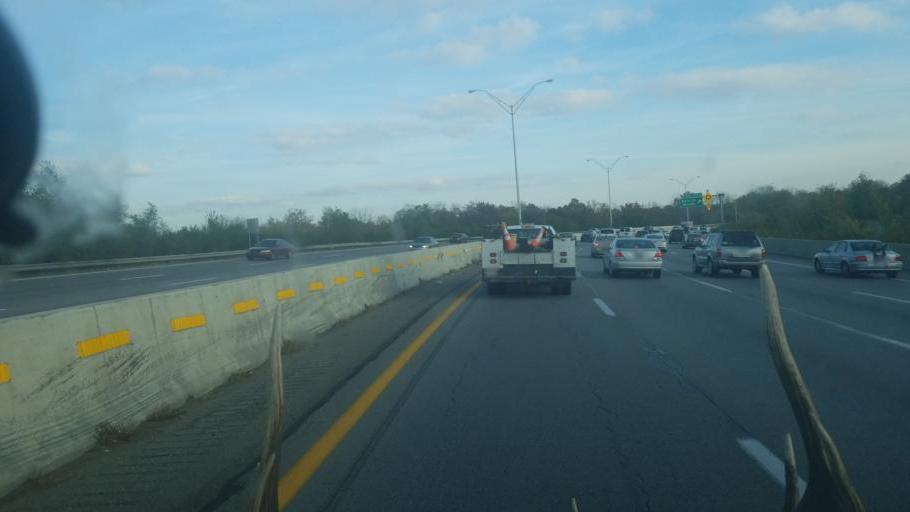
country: US
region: Ohio
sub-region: Franklin County
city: Bexley
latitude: 39.9527
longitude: -82.9462
